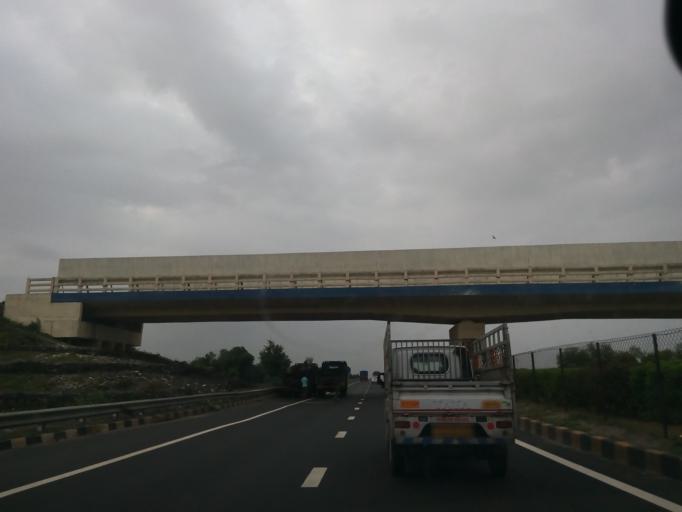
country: IN
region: Gujarat
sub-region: Kheda
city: Mahemdavad
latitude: 22.8586
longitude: 72.8093
